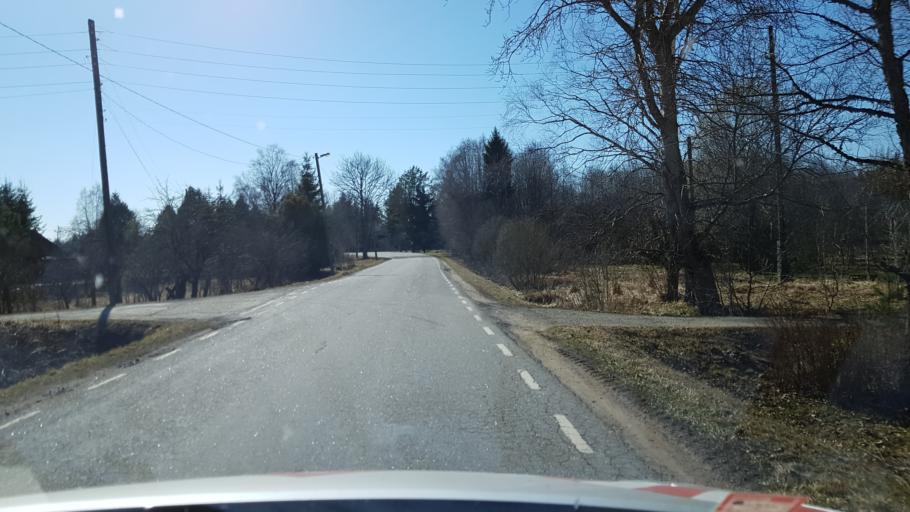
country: EE
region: Laeaene-Virumaa
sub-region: Vaeike-Maarja vald
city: Vaike-Maarja
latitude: 59.0895
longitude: 26.1724
